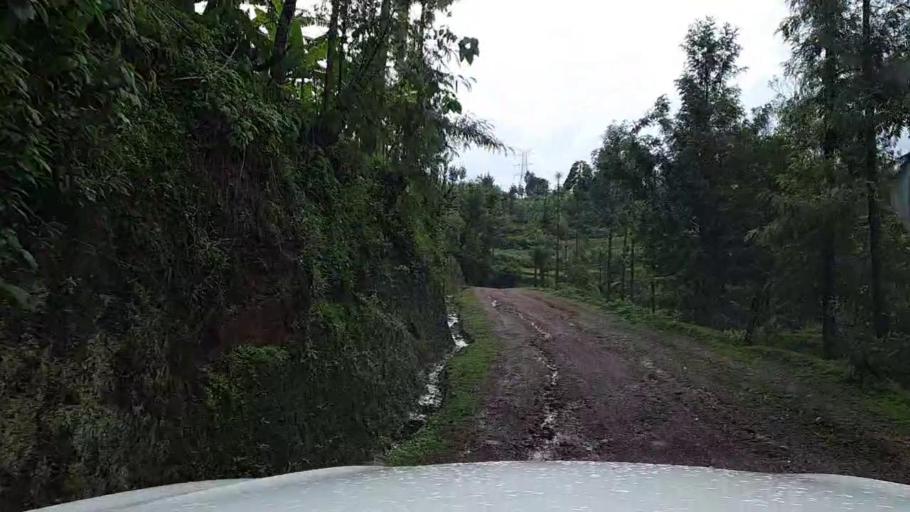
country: RW
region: Northern Province
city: Byumba
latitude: -1.7180
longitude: 29.9106
